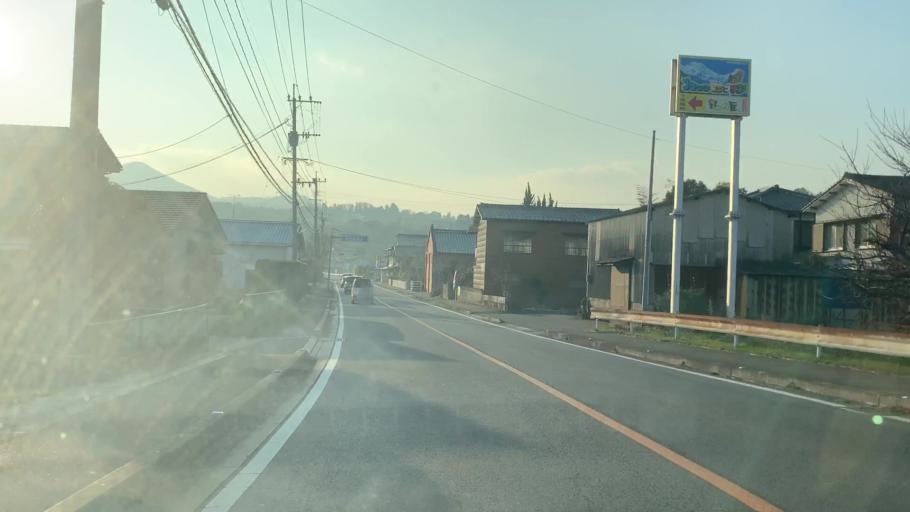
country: JP
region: Saga Prefecture
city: Saga-shi
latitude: 33.2721
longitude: 130.1858
